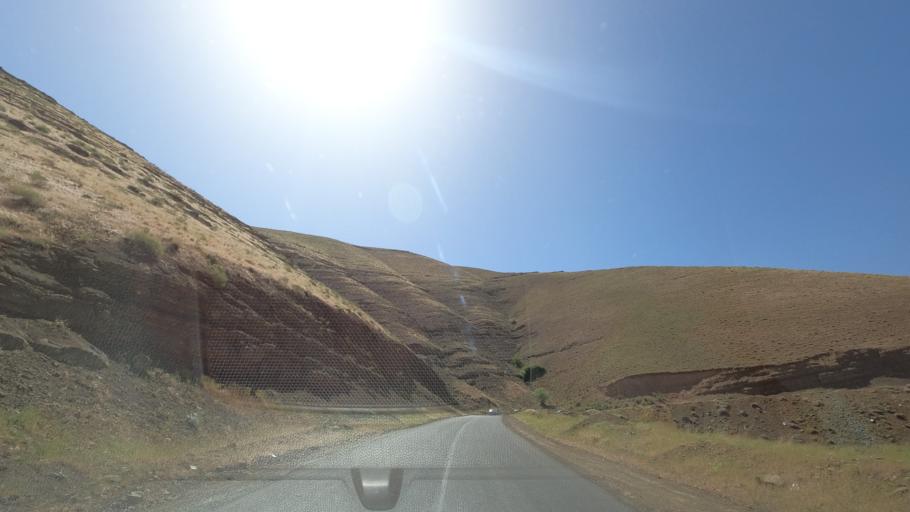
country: IR
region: Alborz
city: Karaj
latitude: 35.9324
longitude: 51.0859
